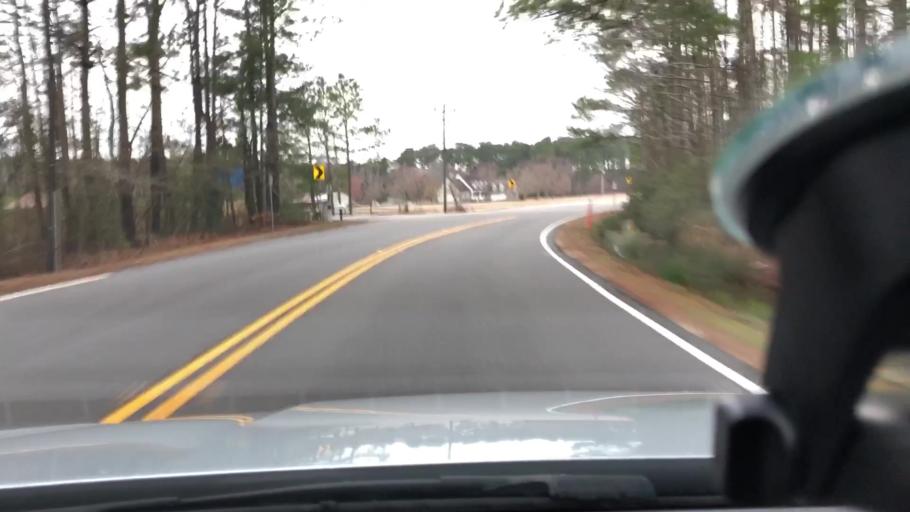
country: US
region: Virginia
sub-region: City of Virginia Beach
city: Virginia Beach
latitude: 36.7311
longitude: -75.9727
